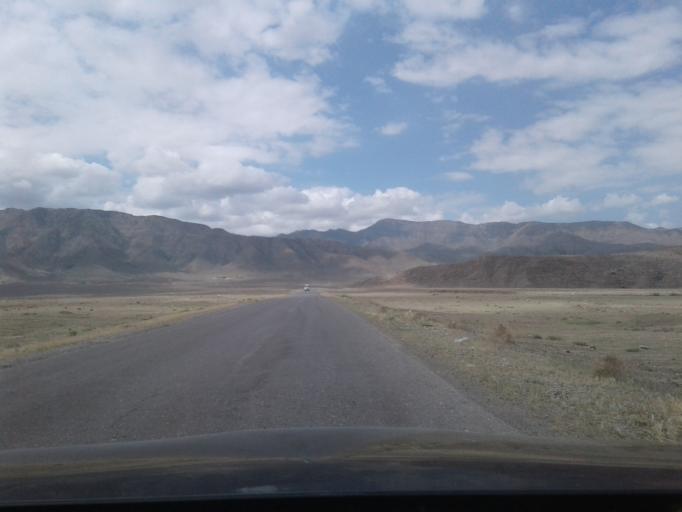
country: TM
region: Ahal
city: Baharly
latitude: 38.5141
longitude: 57.1334
